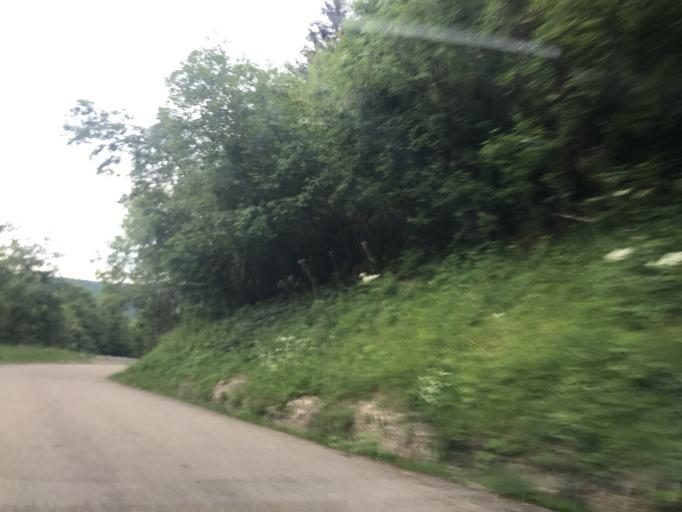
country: FR
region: Rhone-Alpes
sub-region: Departement de l'Isere
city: Saint-Vincent-de-Mercuze
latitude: 45.3804
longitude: 5.9219
